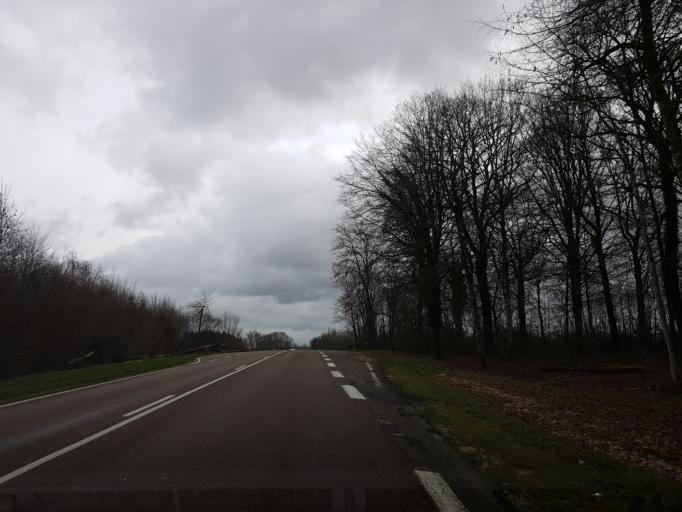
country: FR
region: Champagne-Ardenne
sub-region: Departement de la Haute-Marne
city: Fayl-Billot
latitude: 47.7947
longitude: 5.5696
